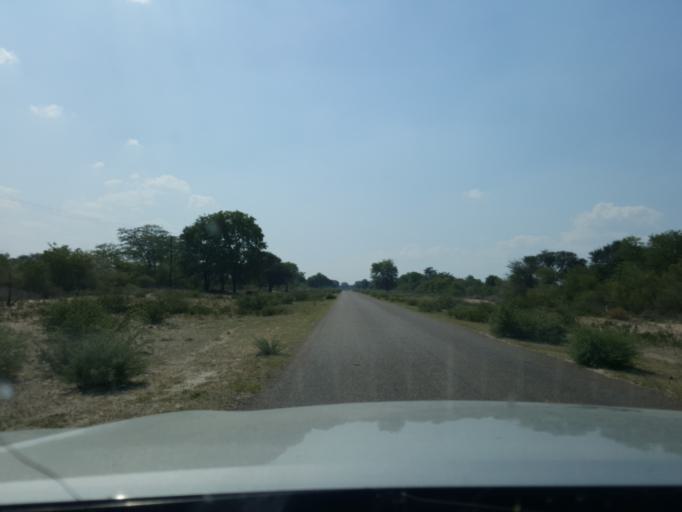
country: BW
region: North West
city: Shakawe
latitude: -18.8832
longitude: 22.2642
